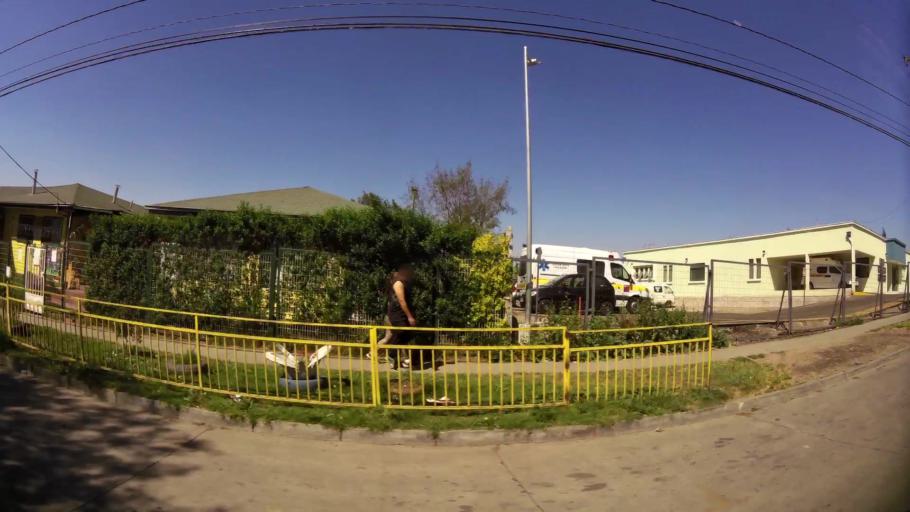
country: CL
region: Santiago Metropolitan
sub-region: Provincia de Santiago
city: Lo Prado
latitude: -33.5005
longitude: -70.7333
